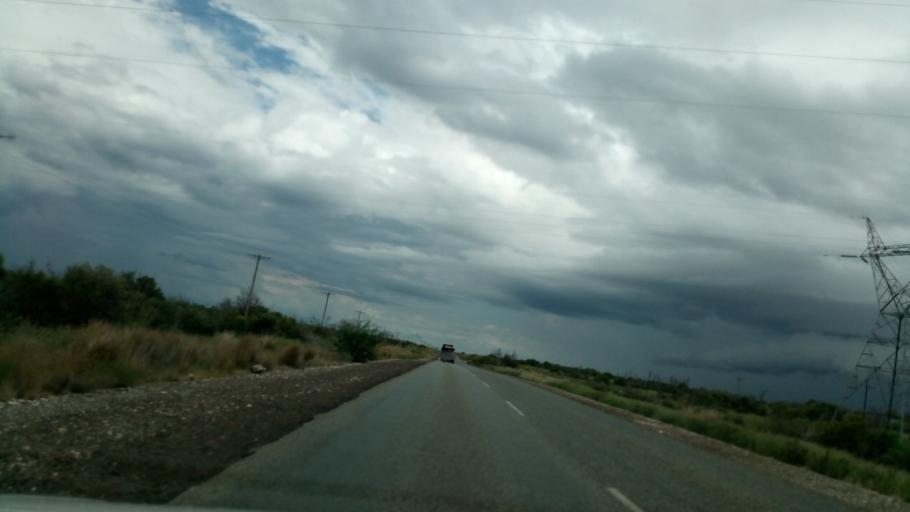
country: ZA
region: Northern Cape
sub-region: Siyanda District Municipality
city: Danielskuil
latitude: -28.2641
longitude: 24.0639
